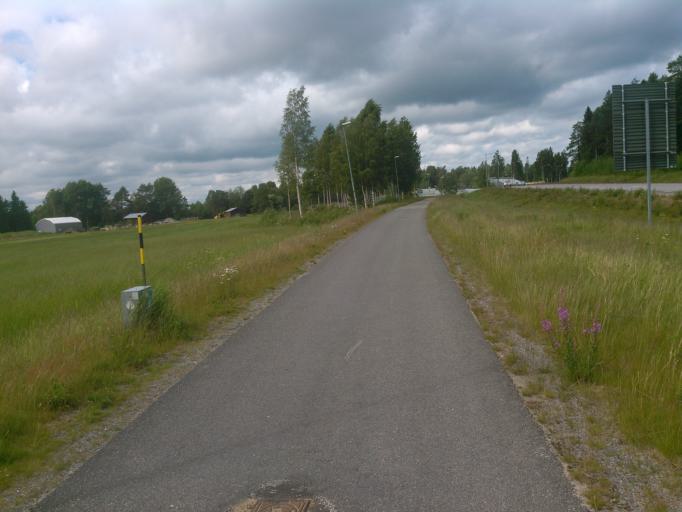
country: SE
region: Vaesterbotten
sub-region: Umea Kommun
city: Roback
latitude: 63.8605
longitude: 20.2018
